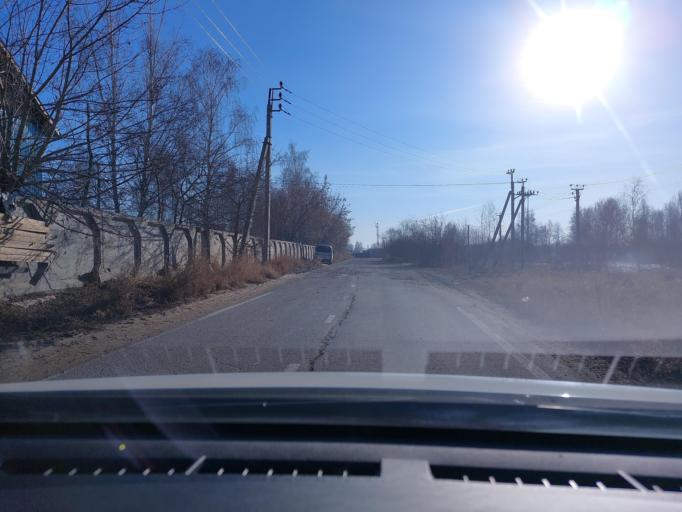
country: RU
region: Irkutsk
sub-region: Irkutskiy Rayon
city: Irkutsk
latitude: 52.3099
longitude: 104.2715
